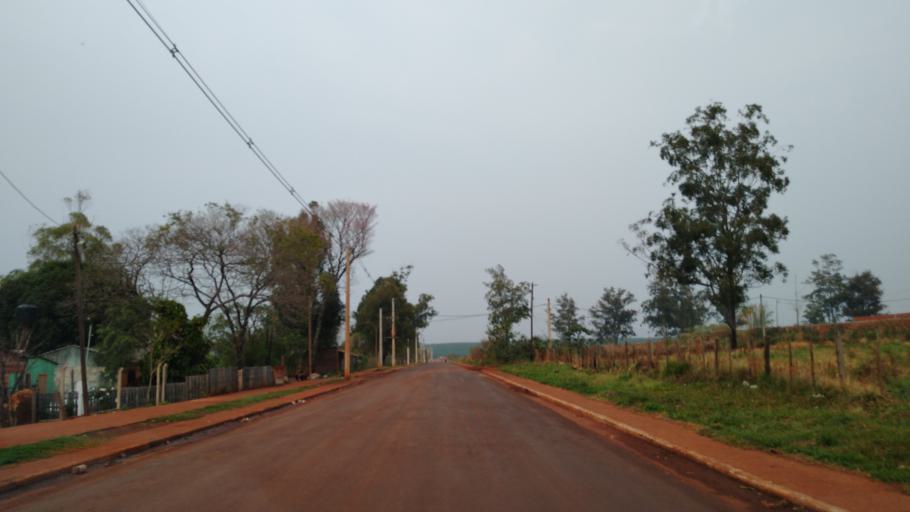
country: AR
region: Misiones
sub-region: Departamento de Capital
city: Posadas
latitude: -27.4472
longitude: -55.9335
